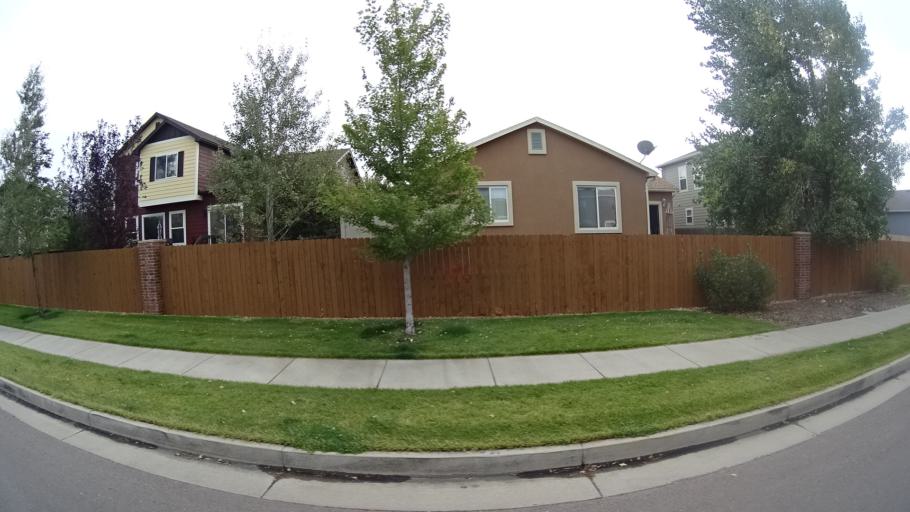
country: US
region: Colorado
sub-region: El Paso County
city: Cimarron Hills
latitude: 38.9233
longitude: -104.6999
